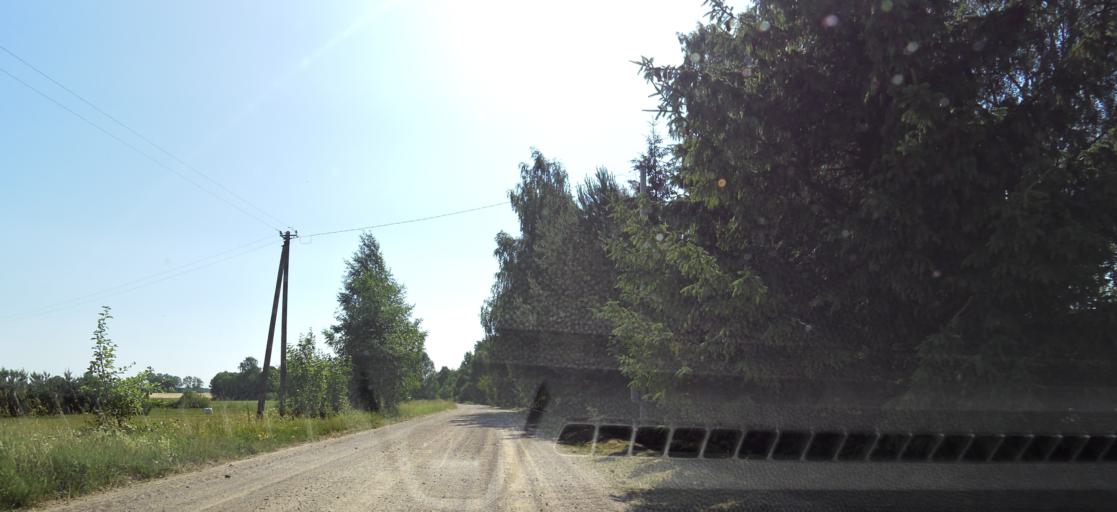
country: LT
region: Panevezys
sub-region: Birzai
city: Birzai
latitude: 56.2455
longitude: 24.8802
